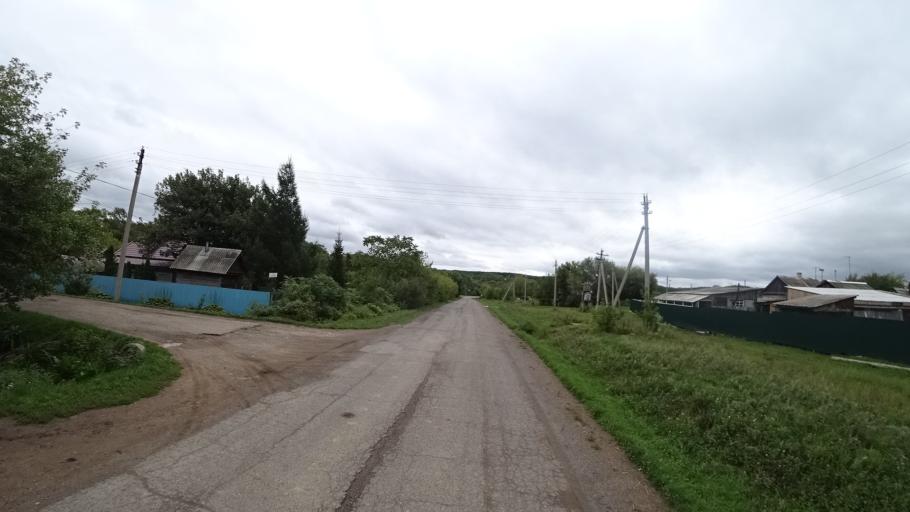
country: RU
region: Primorskiy
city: Chernigovka
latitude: 44.4631
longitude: 132.5908
